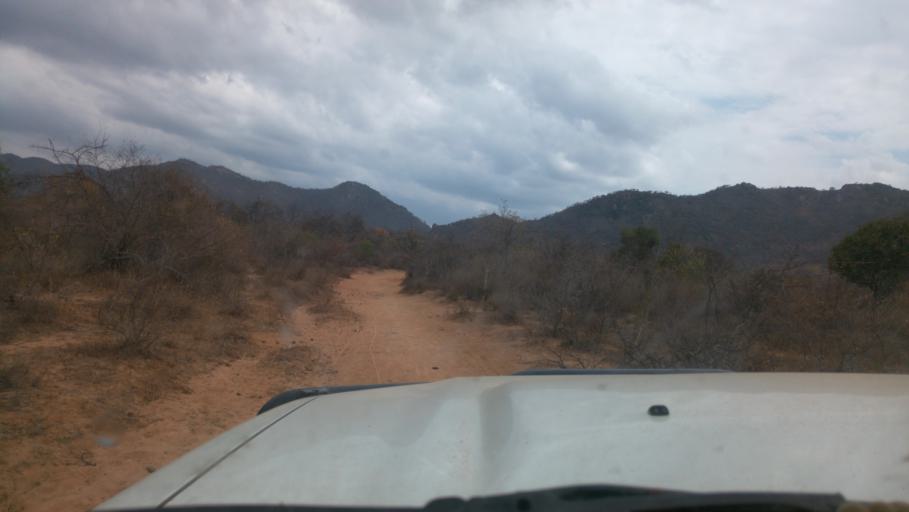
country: KE
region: Kitui
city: Kitui
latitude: -1.8191
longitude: 38.4209
